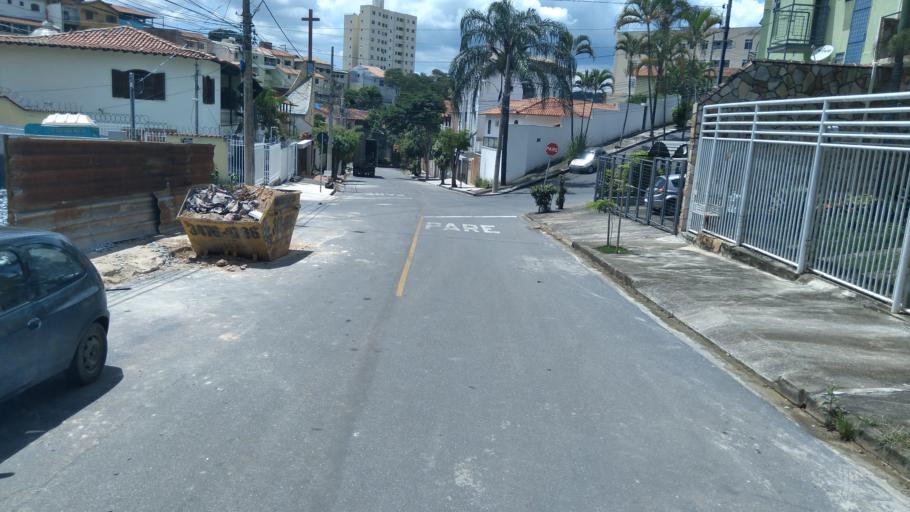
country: BR
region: Minas Gerais
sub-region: Contagem
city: Contagem
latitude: -19.9136
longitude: -44.0075
